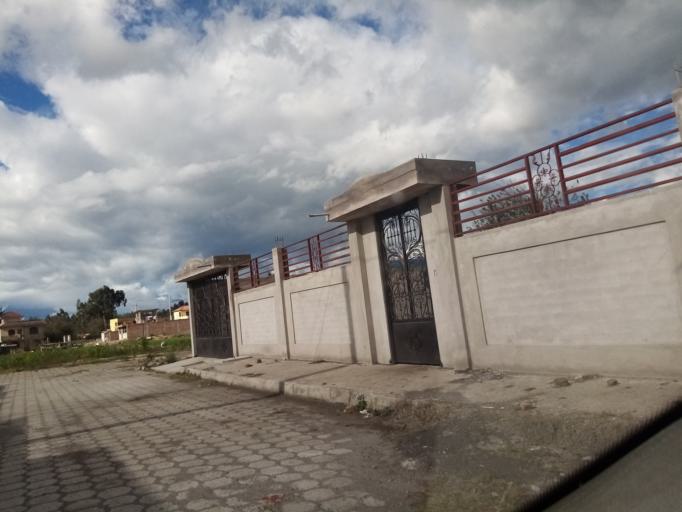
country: EC
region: Chimborazo
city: Riobamba
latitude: -1.6866
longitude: -78.6259
